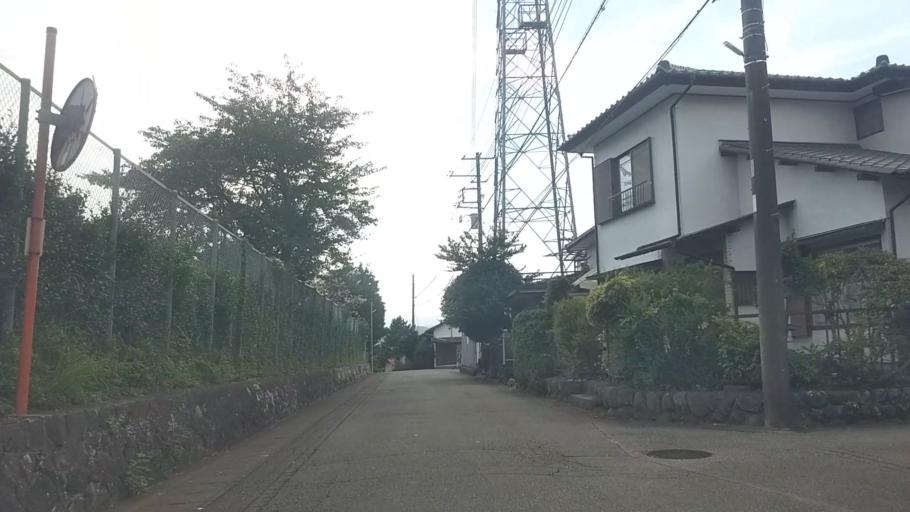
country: JP
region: Shizuoka
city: Ito
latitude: 34.9758
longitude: 138.9509
